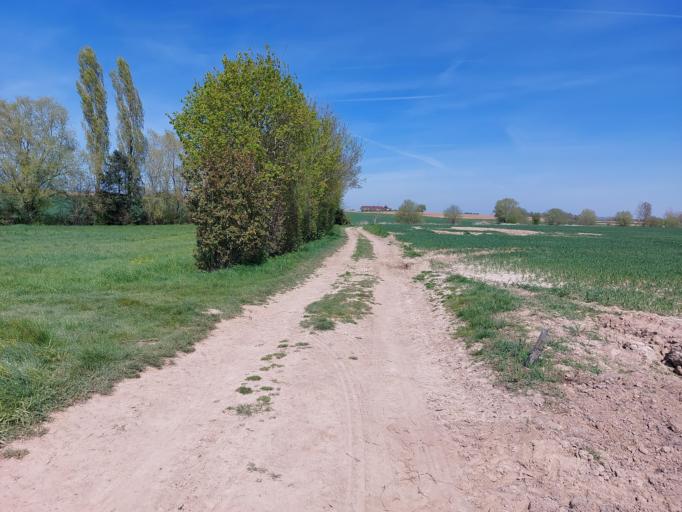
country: BE
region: Wallonia
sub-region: Province du Hainaut
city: Lens
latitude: 50.5835
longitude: 3.9446
